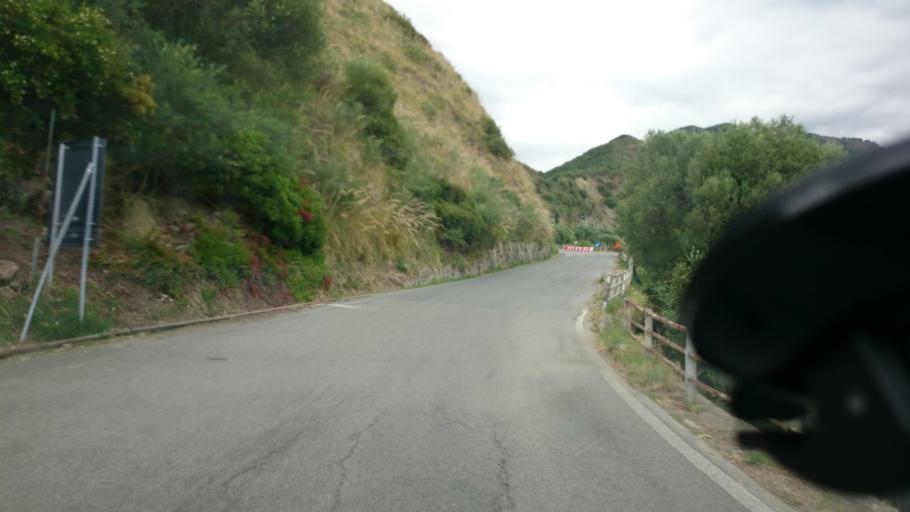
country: IT
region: Campania
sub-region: Provincia di Salerno
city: Ascea
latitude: 40.1270
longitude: 15.2033
